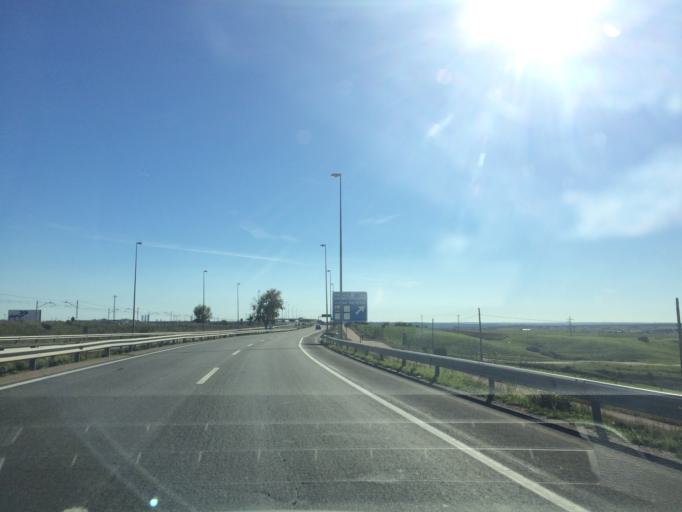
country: ES
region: Madrid
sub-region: Provincia de Madrid
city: Tres Cantos
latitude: 40.6342
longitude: -3.7299
